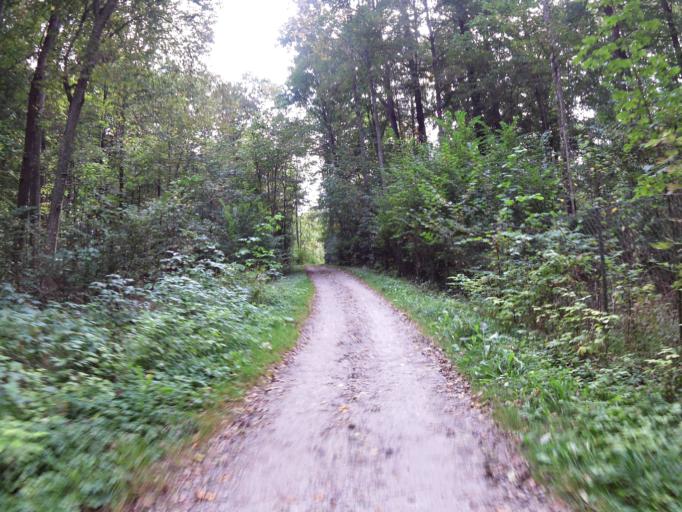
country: DE
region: Bavaria
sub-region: Upper Bavaria
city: Seeshaupt
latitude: 47.8319
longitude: 11.3378
